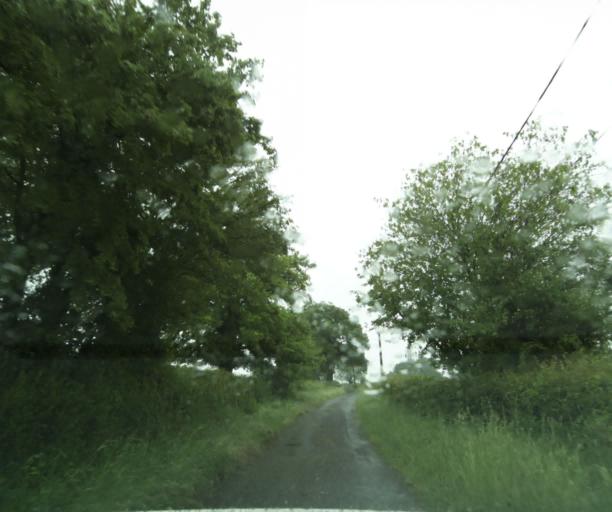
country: FR
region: Bourgogne
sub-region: Departement de Saone-et-Loire
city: Ciry-le-Noble
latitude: 46.5333
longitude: 4.3640
